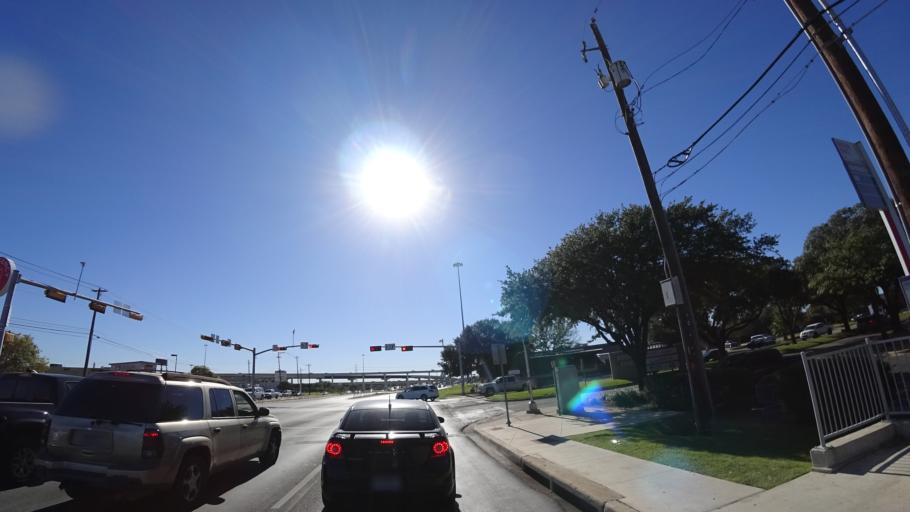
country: US
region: Texas
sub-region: Travis County
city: Rollingwood
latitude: 30.2365
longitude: -97.7925
